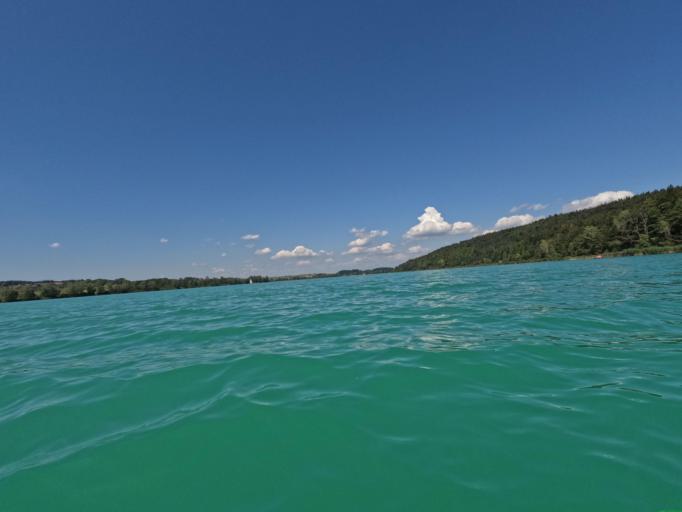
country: DE
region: Bavaria
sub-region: Upper Bavaria
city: Taching am See
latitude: 47.9672
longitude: 12.7449
